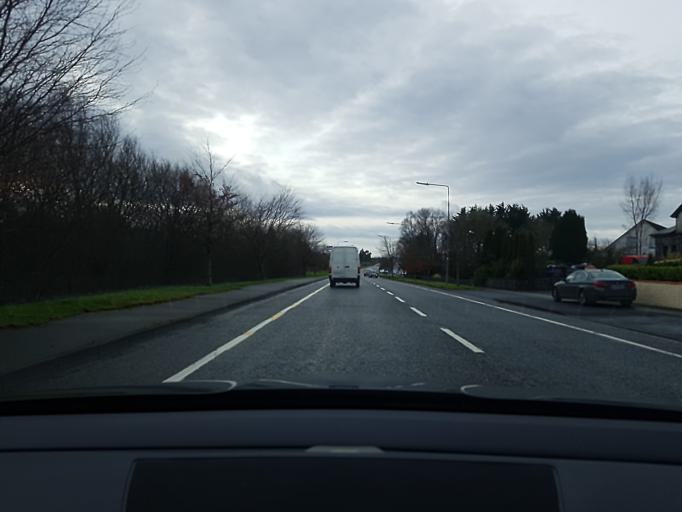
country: IE
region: Connaught
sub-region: Maigh Eo
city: Castlebar
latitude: 53.8416
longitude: -9.2909
